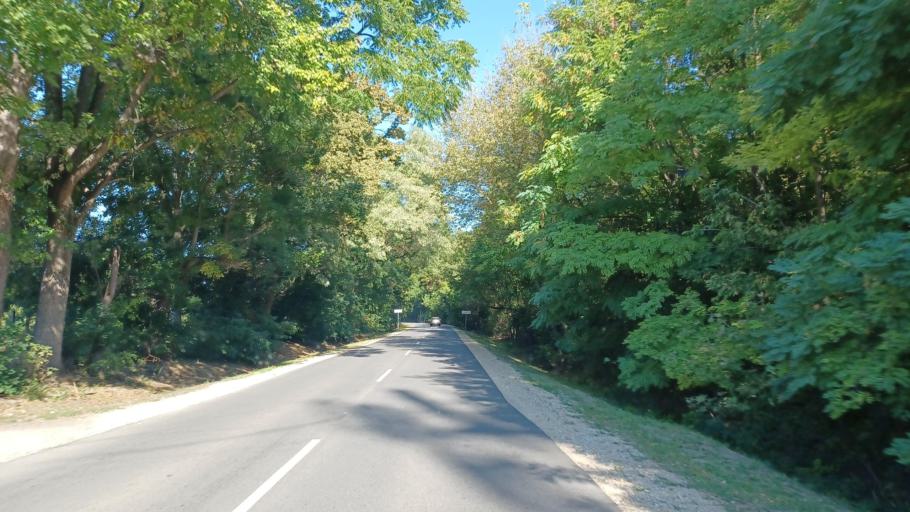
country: HU
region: Tolna
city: Nemetker
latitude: 46.6755
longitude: 18.8128
